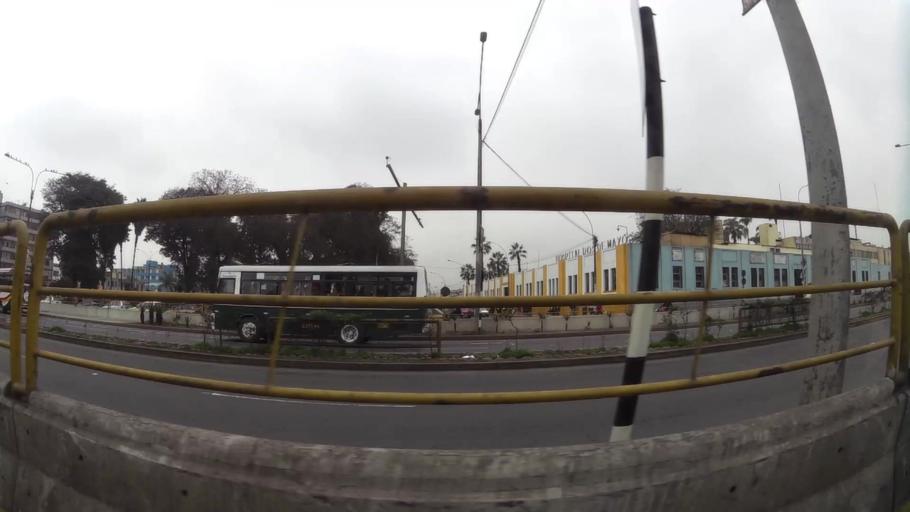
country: PE
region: Lima
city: Lima
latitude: -12.0574
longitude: -77.0165
